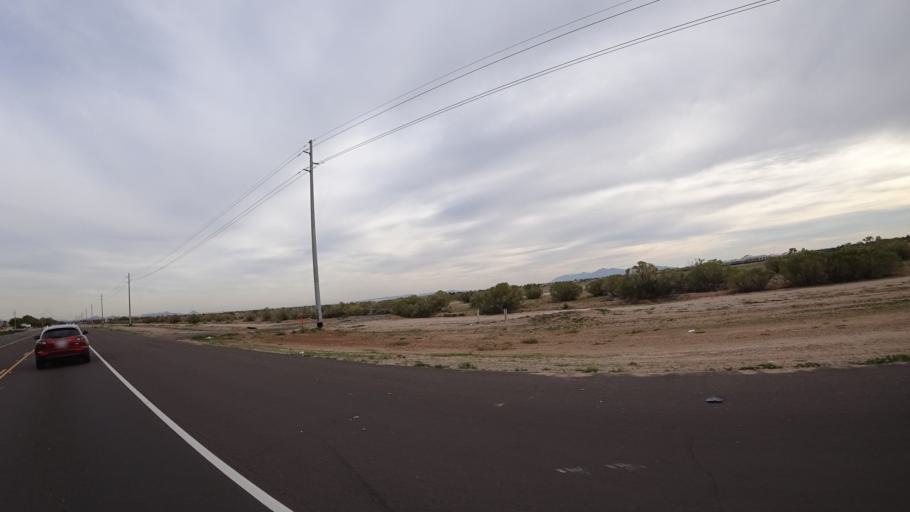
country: US
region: Arizona
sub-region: Maricopa County
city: Surprise
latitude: 33.6092
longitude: -112.3713
